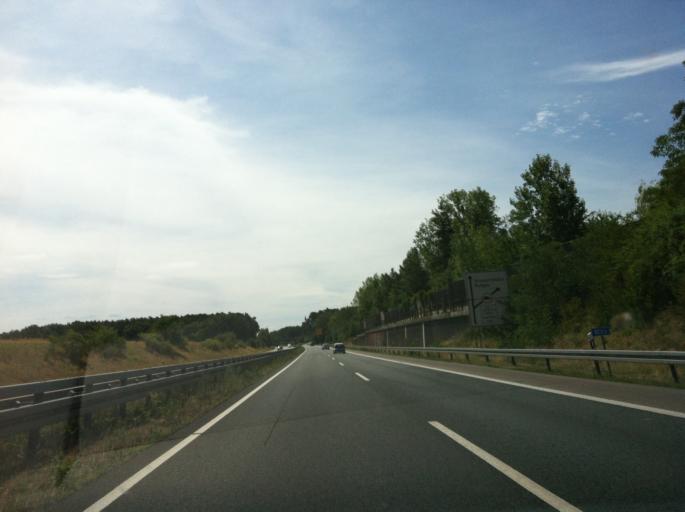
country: DE
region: Hesse
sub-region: Regierungsbezirk Darmstadt
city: Rodgau
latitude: 50.0437
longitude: 8.8900
